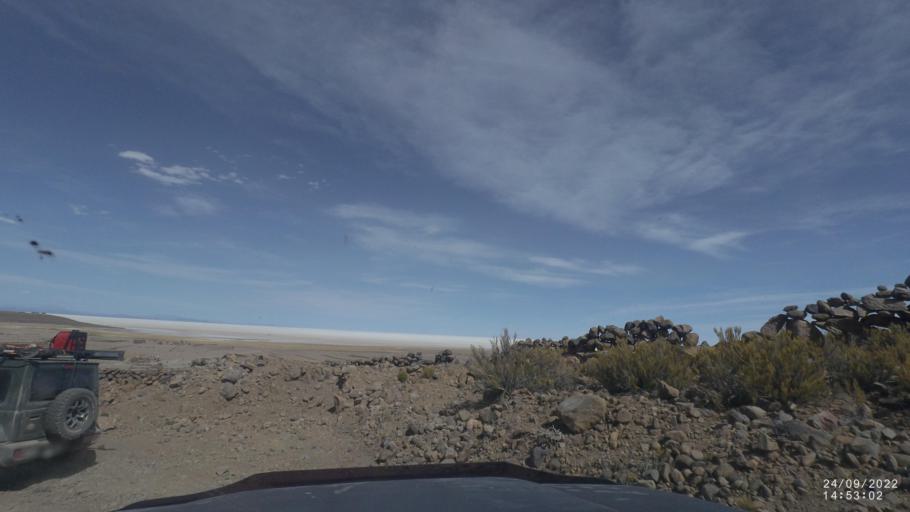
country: BO
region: Potosi
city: Colchani
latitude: -19.8541
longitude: -67.5793
